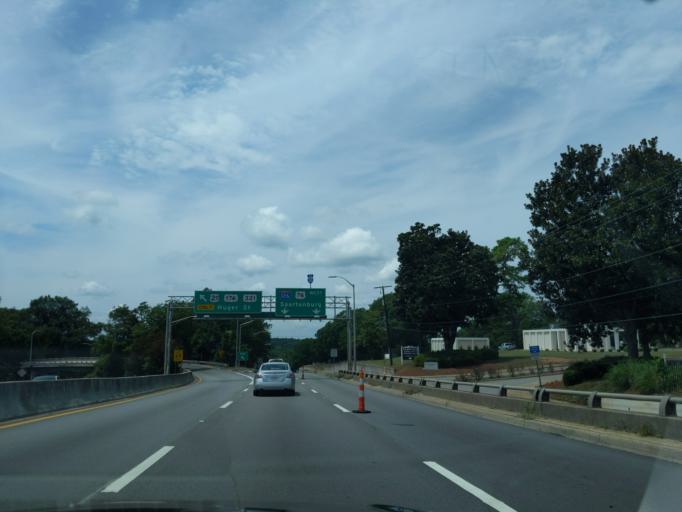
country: US
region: South Carolina
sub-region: Richland County
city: Columbia
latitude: 34.0104
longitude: -81.0489
